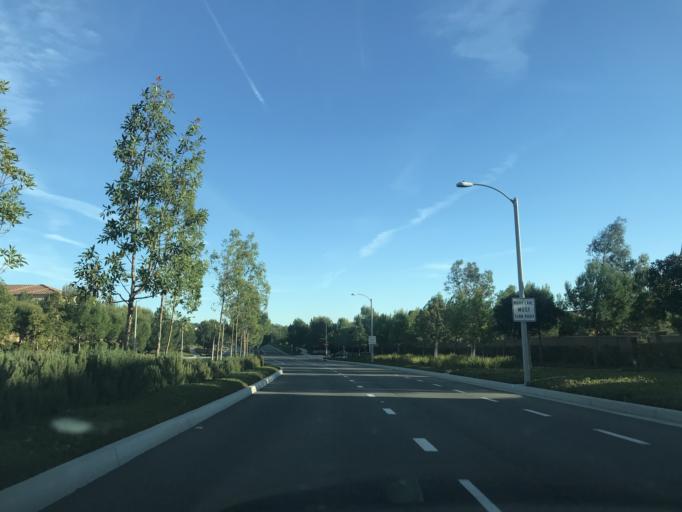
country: US
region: California
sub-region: Orange County
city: North Tustin
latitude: 33.7110
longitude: -117.7432
